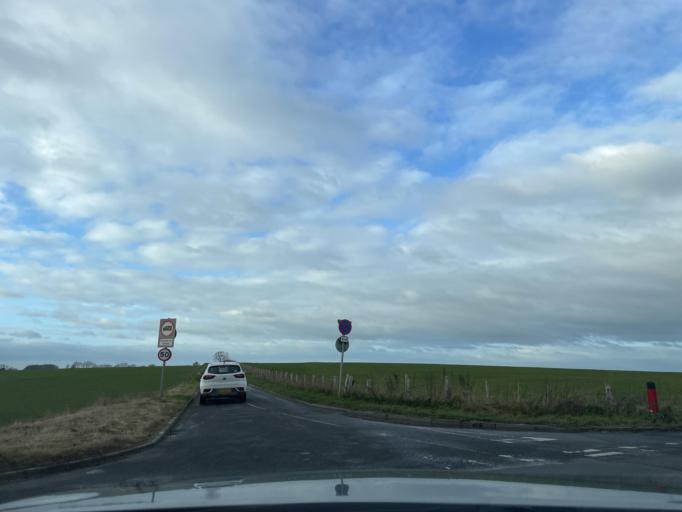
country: GB
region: England
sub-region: Borough of Swindon
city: Wroughton
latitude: 51.5124
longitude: -1.8130
